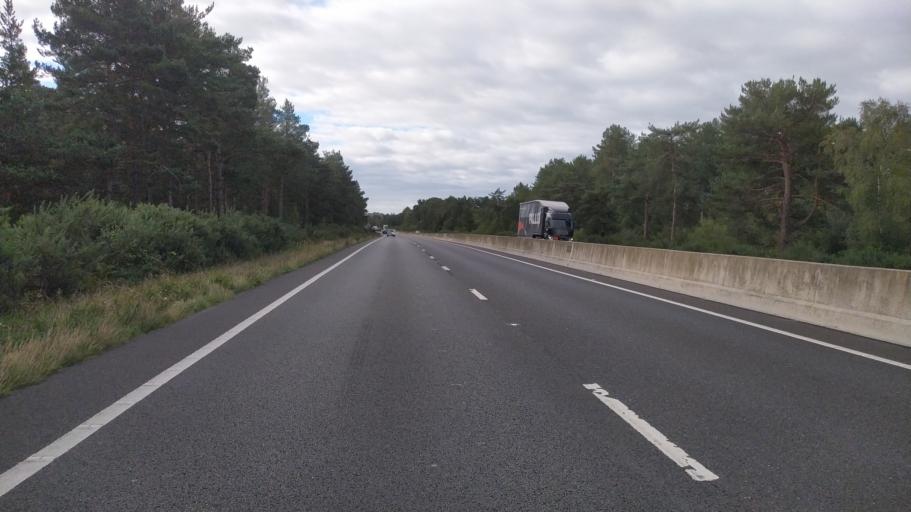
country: GB
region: England
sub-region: Dorset
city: St Leonards
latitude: 50.7901
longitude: -1.8144
